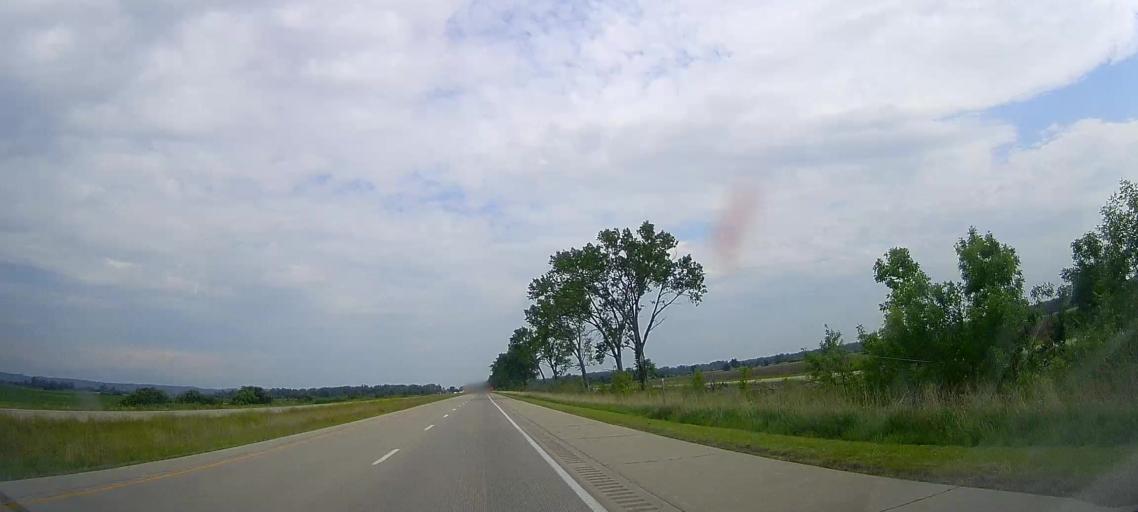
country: US
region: Nebraska
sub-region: Burt County
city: Tekamah
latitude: 41.8338
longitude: -96.0833
